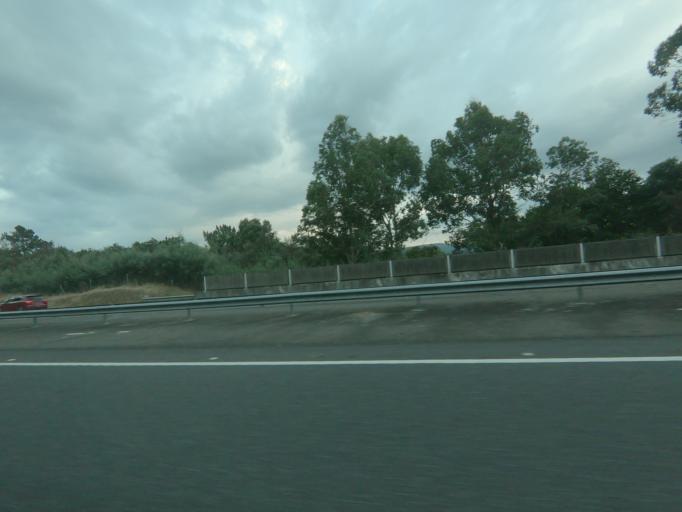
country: ES
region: Galicia
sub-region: Provincia de Ourense
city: Cenlle
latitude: 42.3360
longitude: -8.0494
